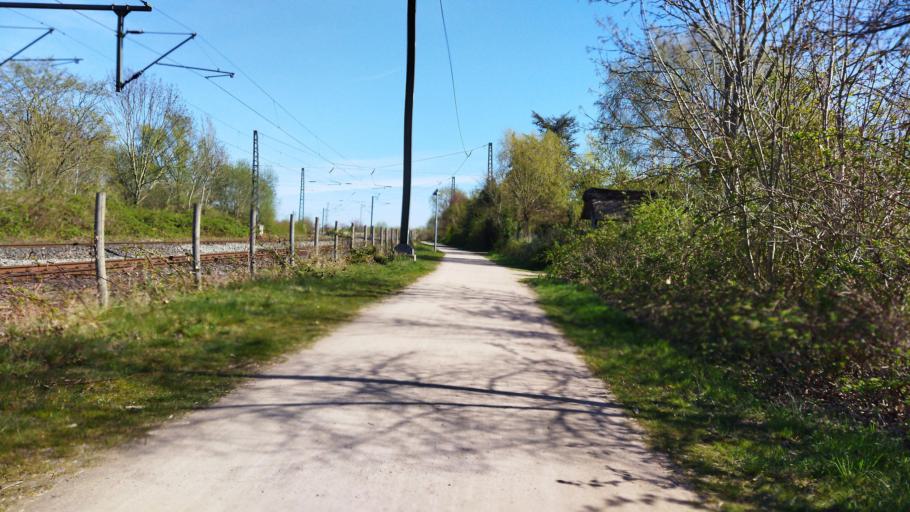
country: DE
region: Lower Saxony
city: Elsfleth
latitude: 53.2307
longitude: 8.4620
